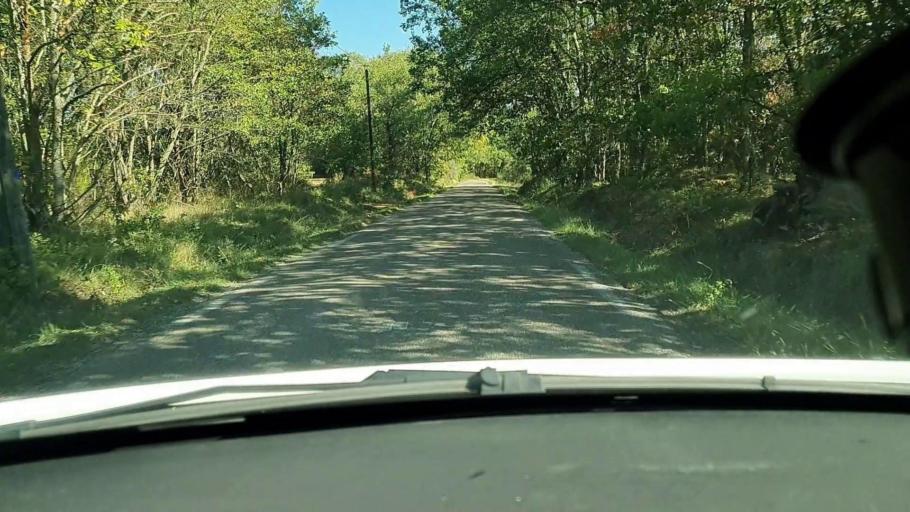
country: FR
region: Languedoc-Roussillon
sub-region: Departement du Gard
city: Saint-Julien-de-Peyrolas
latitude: 44.2743
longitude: 4.5355
